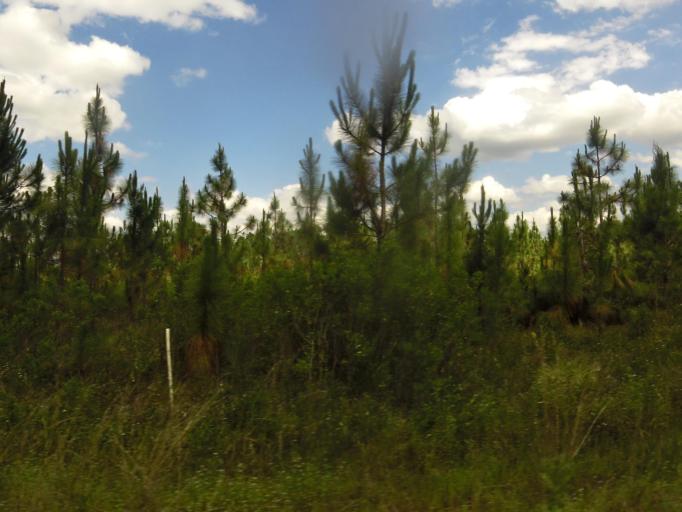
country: US
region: Florida
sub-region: Clay County
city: Asbury Lake
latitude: 29.8903
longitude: -81.8510
